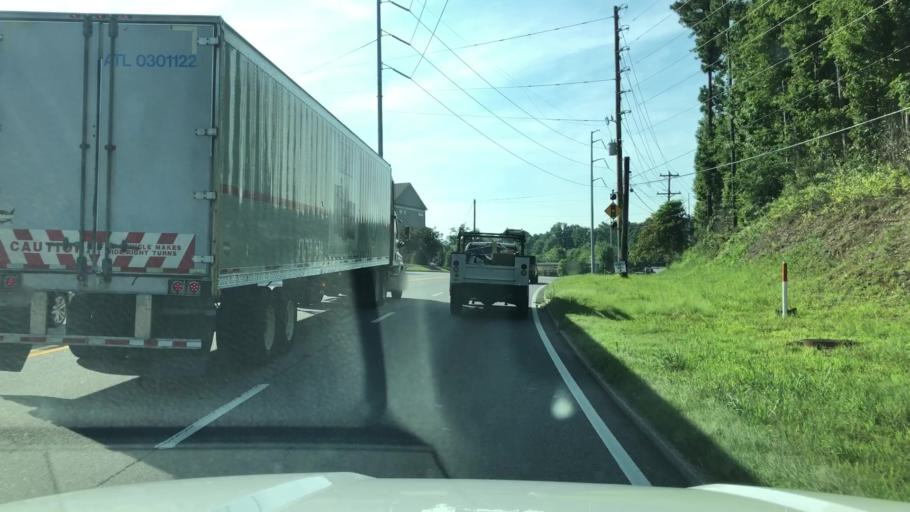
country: US
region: Georgia
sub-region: Fulton County
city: Roswell
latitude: 34.0073
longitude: -84.2987
